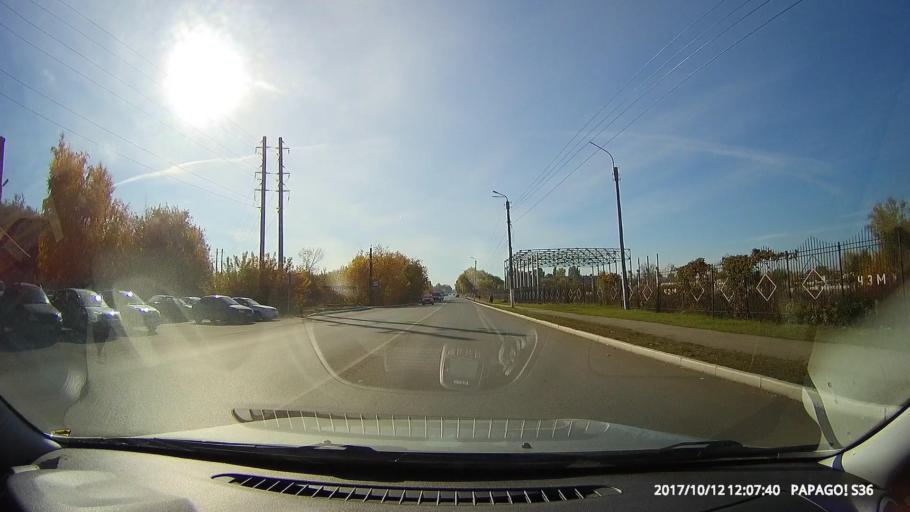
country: RU
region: Samara
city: Chapayevsk
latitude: 52.9661
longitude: 49.7002
